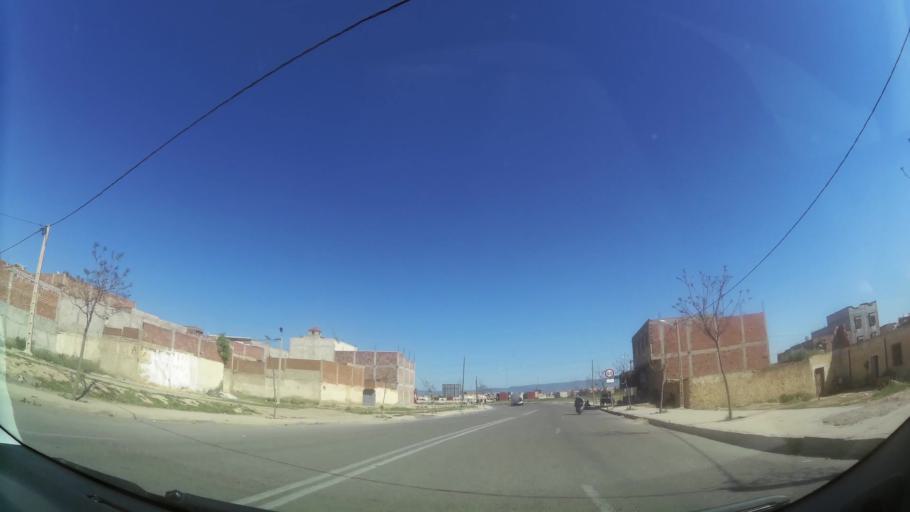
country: MA
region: Oriental
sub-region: Oujda-Angad
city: Oujda
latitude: 34.7212
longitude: -1.9053
